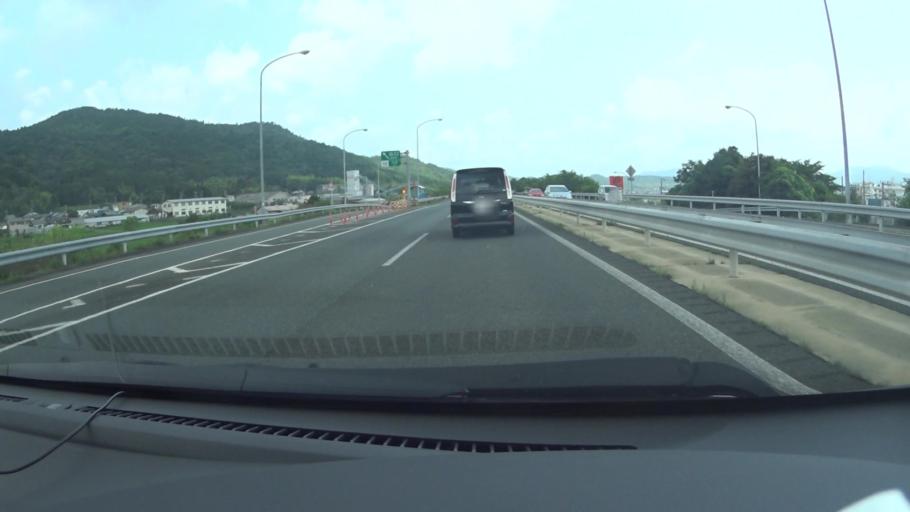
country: JP
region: Kyoto
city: Kameoka
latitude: 35.0288
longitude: 135.5463
